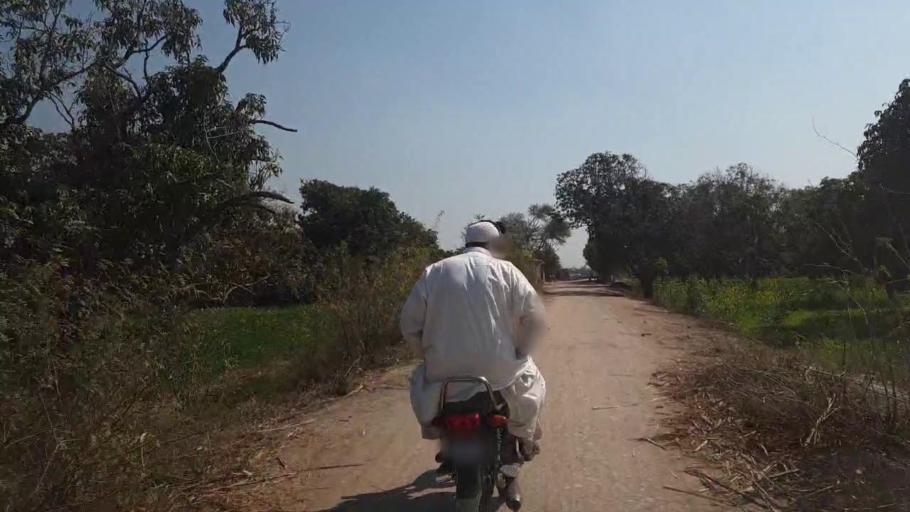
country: PK
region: Sindh
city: Tando Jam
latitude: 25.3288
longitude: 68.6312
